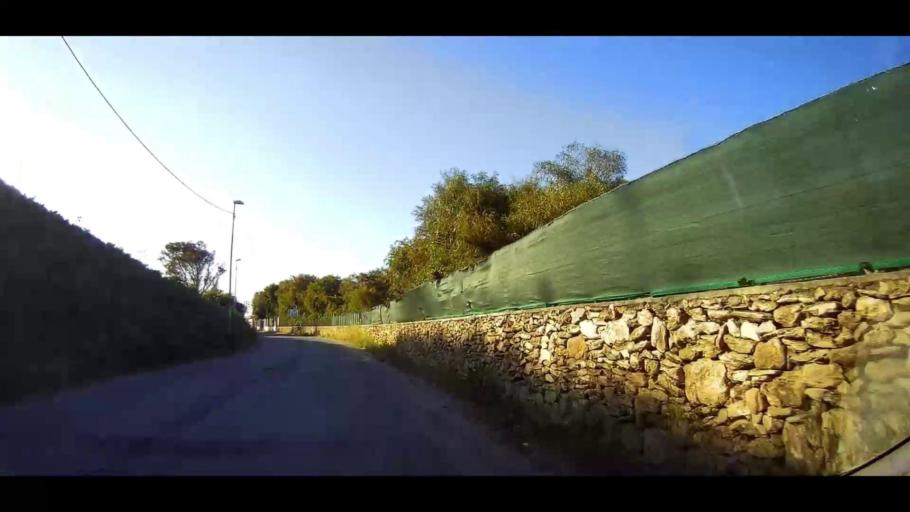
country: IT
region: Calabria
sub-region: Provincia di Crotone
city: Crotone
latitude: 39.0474
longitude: 17.1453
